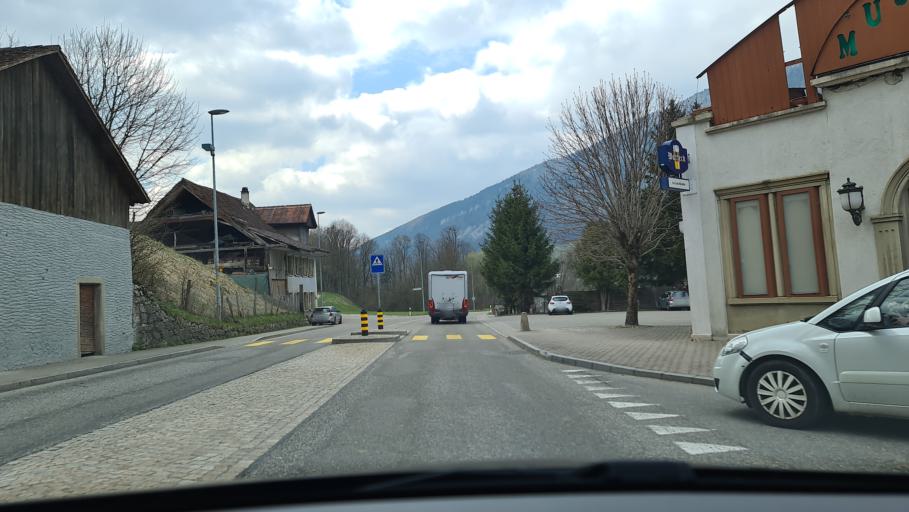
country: CH
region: Bern
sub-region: Jura bernois
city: Moutier
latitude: 47.2826
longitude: 7.4372
